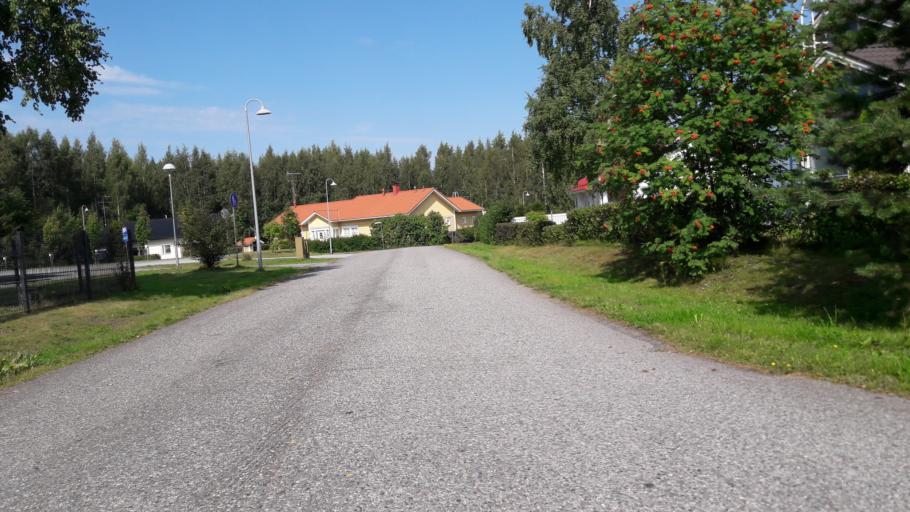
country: FI
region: North Karelia
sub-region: Joensuu
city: Joensuu
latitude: 62.5283
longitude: 29.8415
